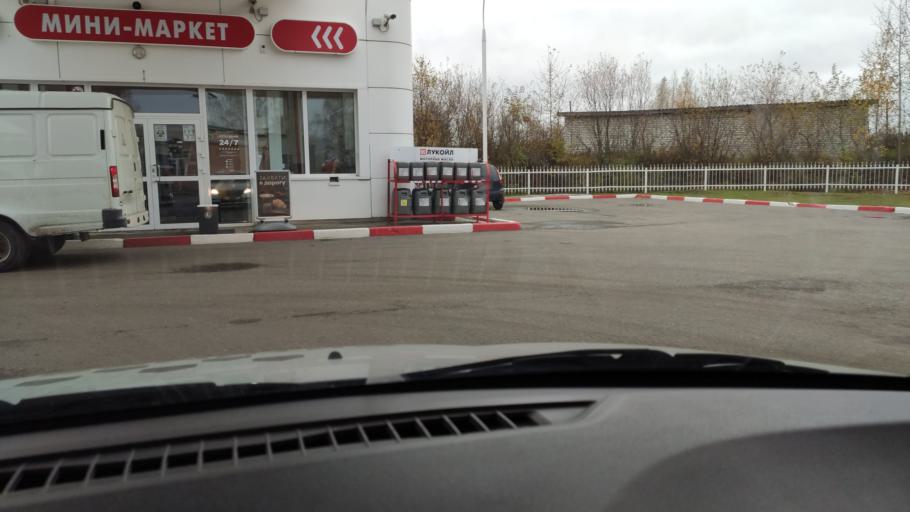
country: RU
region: Kirov
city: Slobodskoy
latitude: 58.7186
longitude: 50.1755
